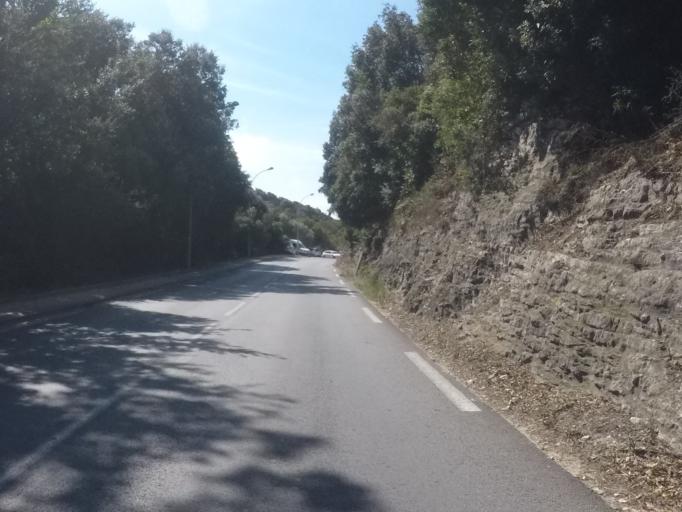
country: FR
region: Corsica
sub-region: Departement de la Corse-du-Sud
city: Bonifacio
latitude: 41.3973
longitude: 9.1635
